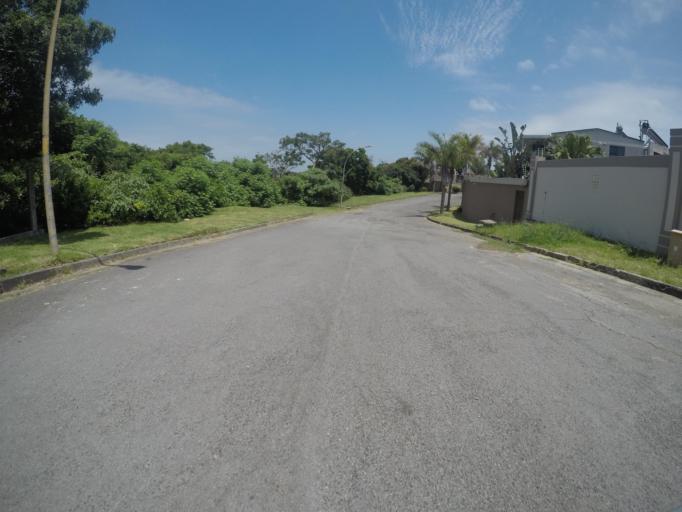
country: ZA
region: Eastern Cape
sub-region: Buffalo City Metropolitan Municipality
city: East London
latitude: -32.9966
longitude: 27.9228
